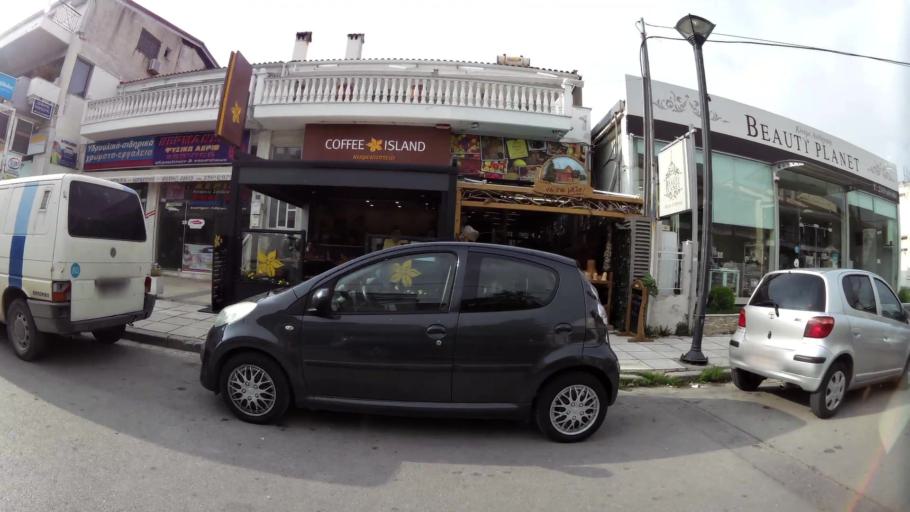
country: GR
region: Central Macedonia
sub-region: Nomos Thessalonikis
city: Oraiokastro
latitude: 40.7308
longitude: 22.9191
